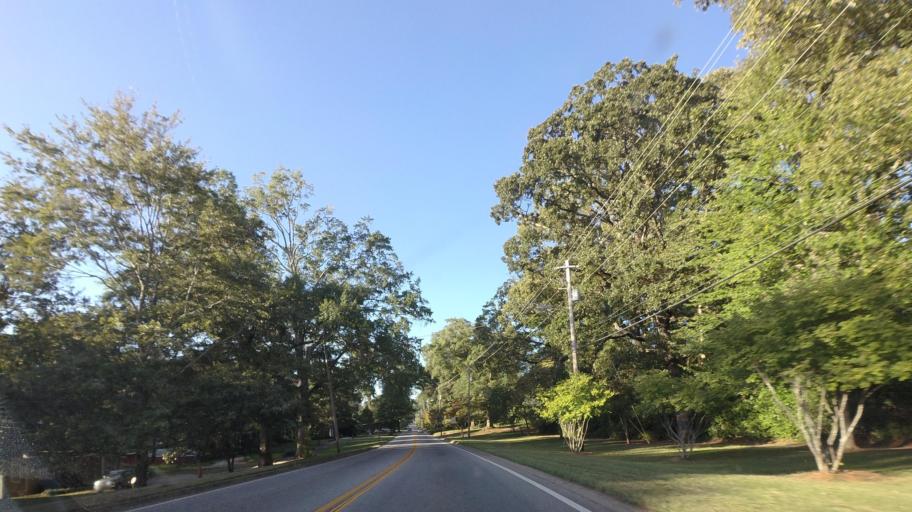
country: US
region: Georgia
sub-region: Spalding County
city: Griffin
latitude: 33.2370
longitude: -84.2641
